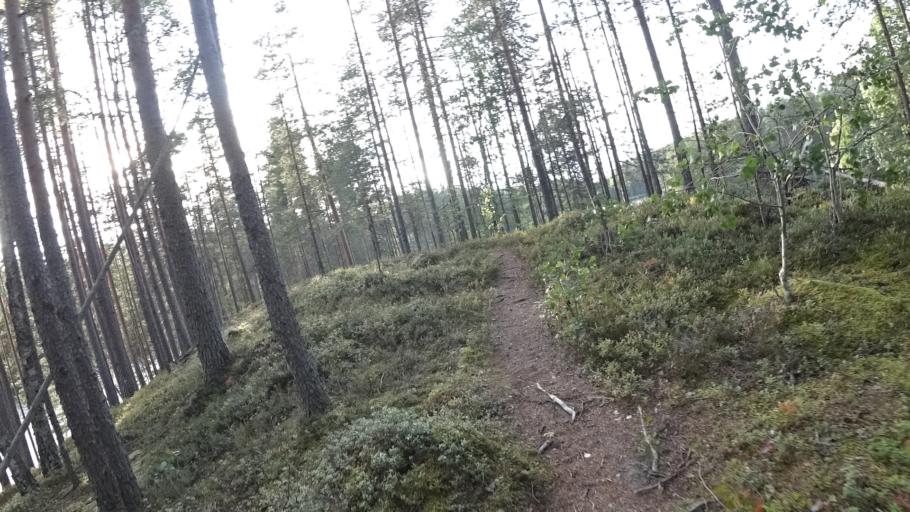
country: FI
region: North Karelia
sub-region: Joensuu
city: Ilomantsi
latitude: 62.5788
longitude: 31.1621
